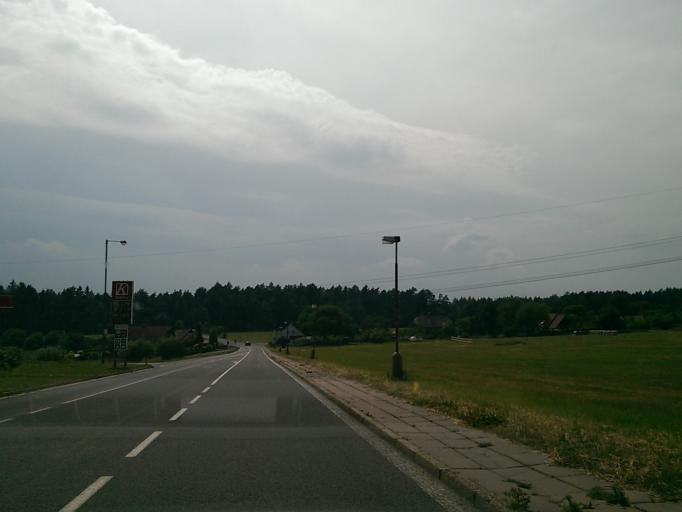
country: CZ
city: Bila Tremesna
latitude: 50.4240
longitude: 15.7300
